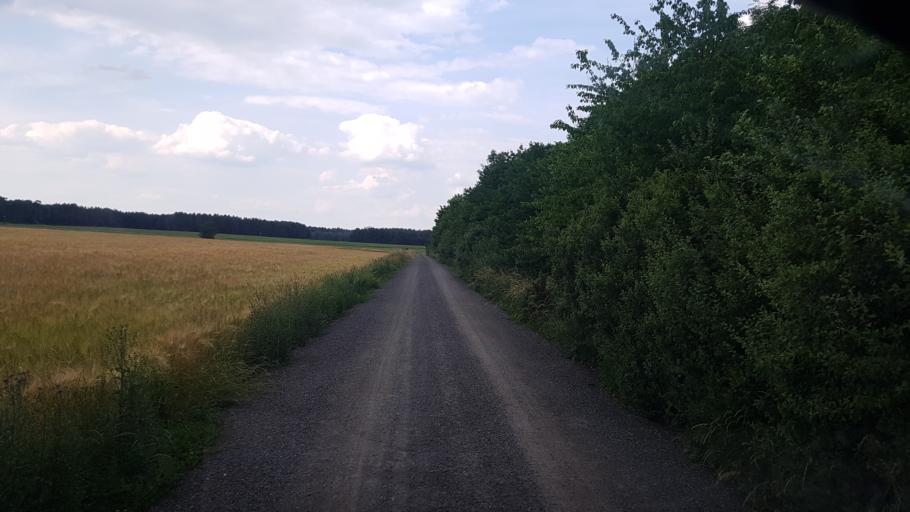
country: DE
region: Brandenburg
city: Plessa
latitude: 51.5390
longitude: 13.6402
